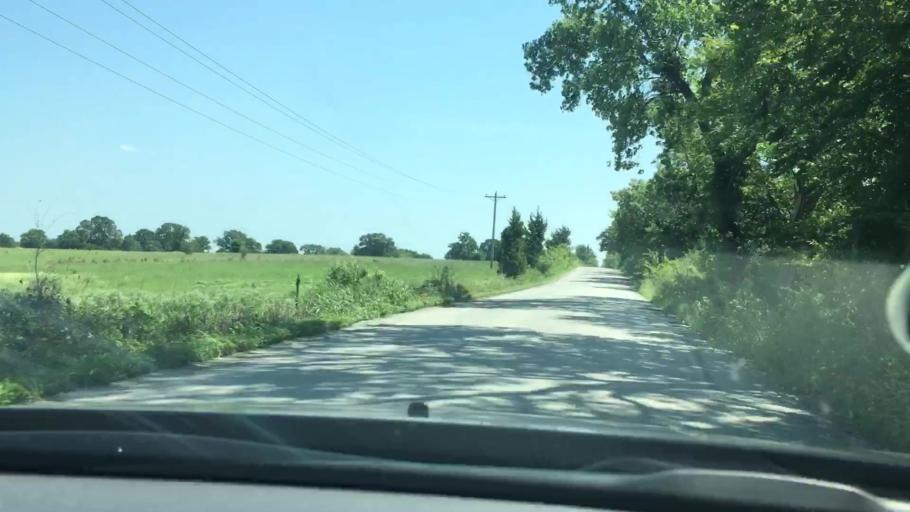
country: US
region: Oklahoma
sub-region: Bryan County
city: Durant
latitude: 34.2588
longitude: -96.3930
